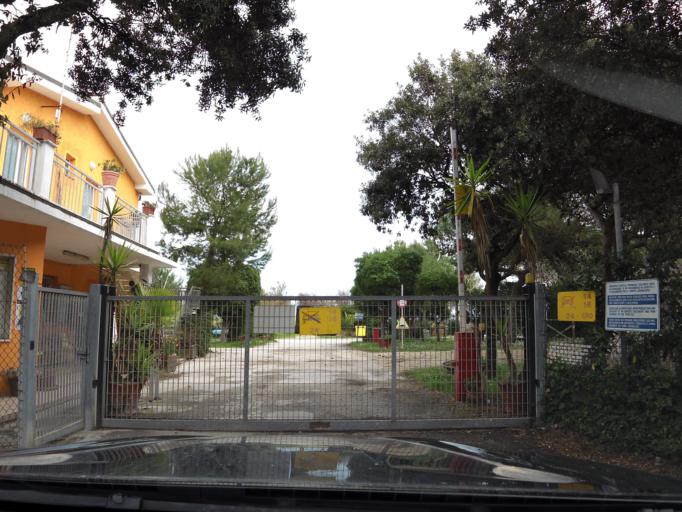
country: IT
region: The Marches
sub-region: Provincia di Macerata
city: Porto Recanati
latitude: 43.4169
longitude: 13.6723
